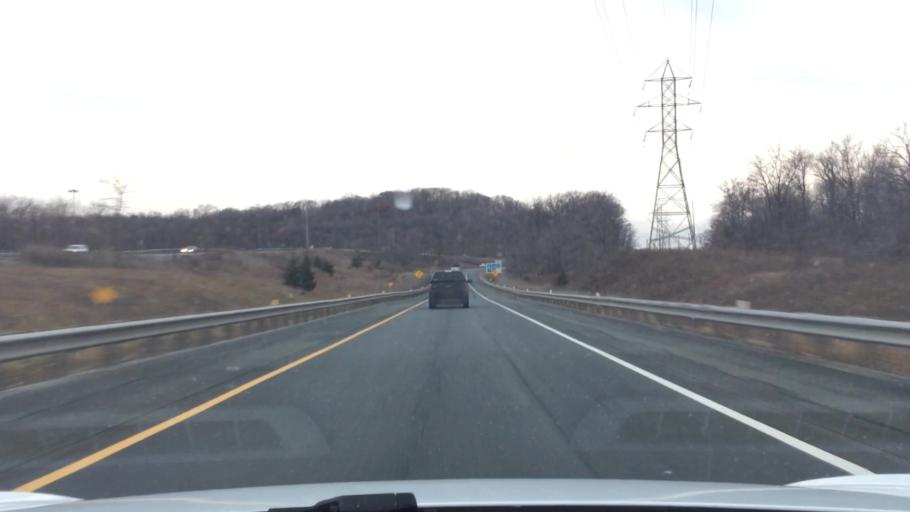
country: CA
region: Ontario
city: Thorold
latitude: 43.1526
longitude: -79.1454
